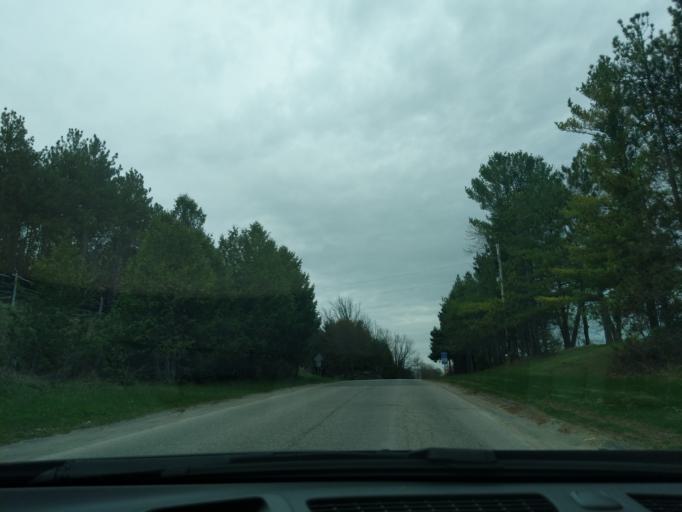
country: CA
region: Ontario
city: Orangeville
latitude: 44.0156
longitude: -79.9676
